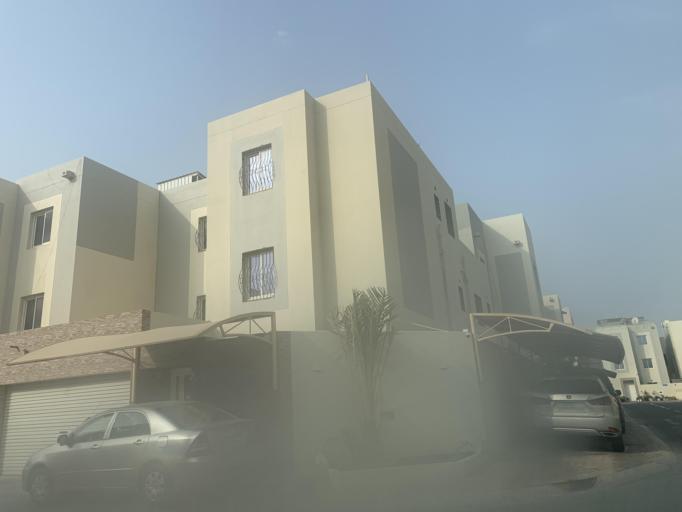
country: BH
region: Manama
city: Jidd Hafs
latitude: 26.2273
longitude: 50.4534
